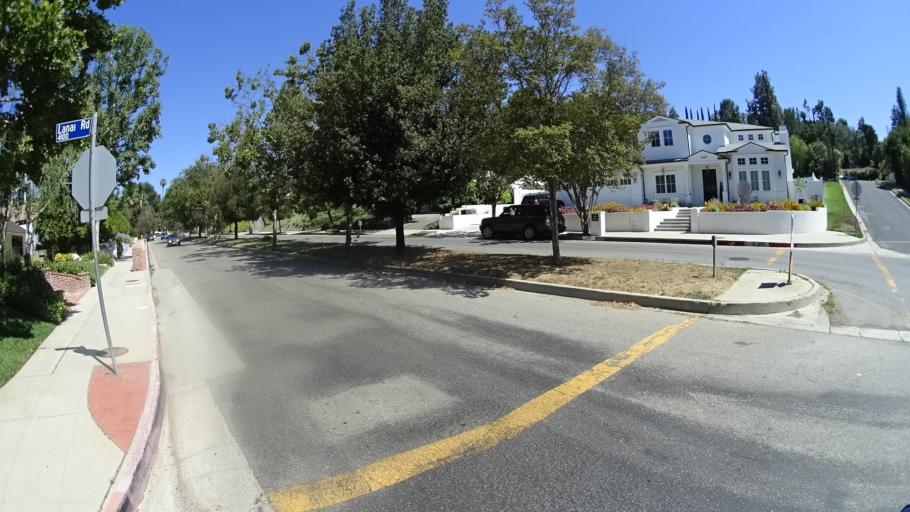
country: US
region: California
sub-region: Los Angeles County
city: Sherman Oaks
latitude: 34.1465
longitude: -118.4931
